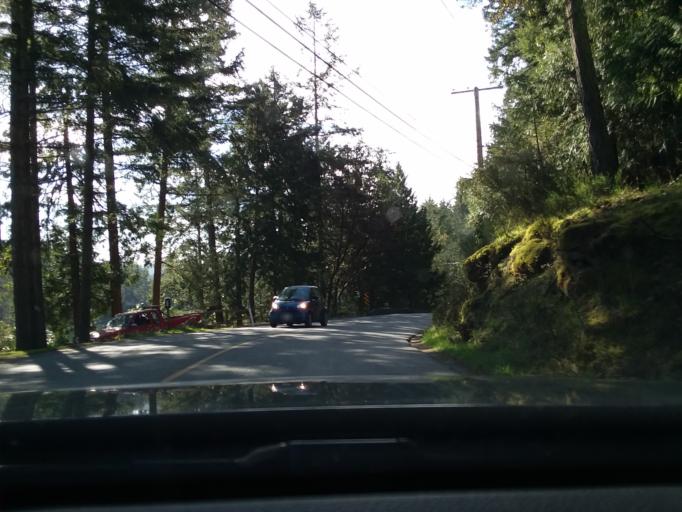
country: CA
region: British Columbia
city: North Saanich
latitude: 48.8820
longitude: -123.3265
